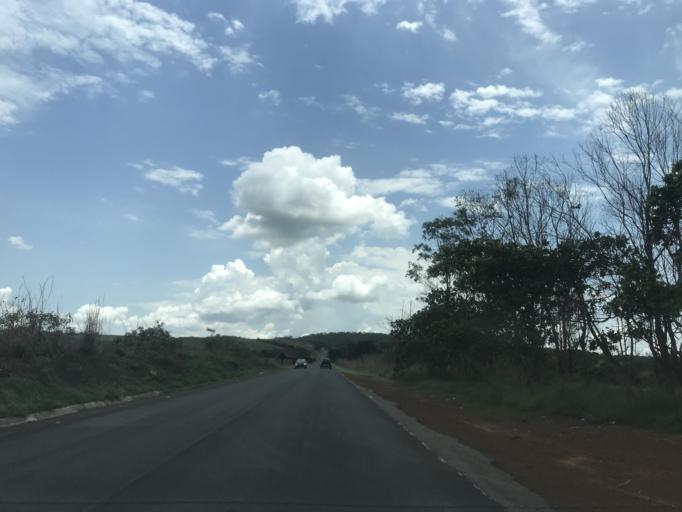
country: BR
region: Goias
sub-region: Vianopolis
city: Vianopolis
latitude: -16.9488
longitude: -48.5902
